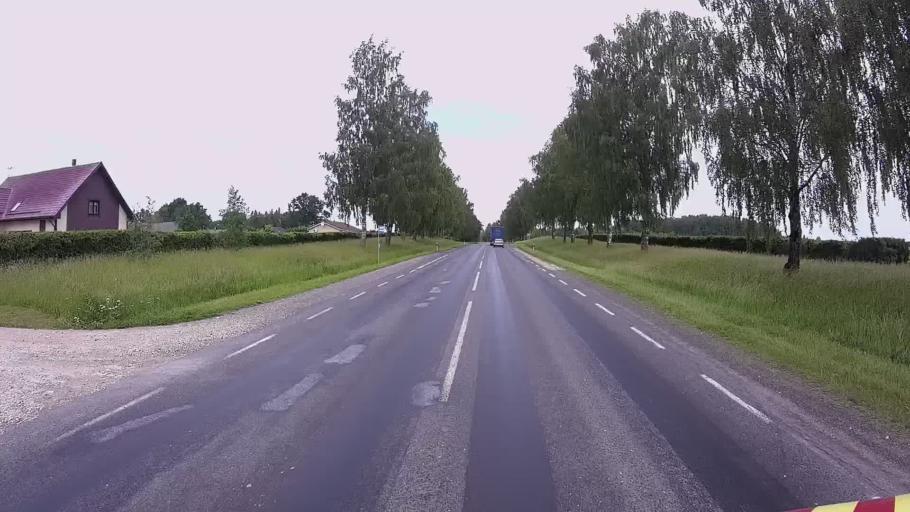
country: EE
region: Viljandimaa
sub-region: Viljandi linn
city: Viljandi
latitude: 58.3073
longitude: 25.5734
